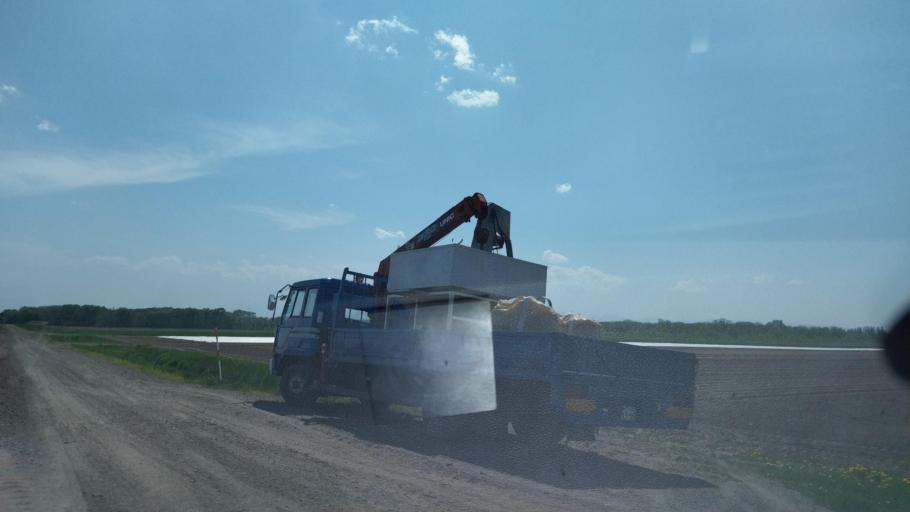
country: JP
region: Hokkaido
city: Otofuke
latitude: 43.1420
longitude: 143.2212
